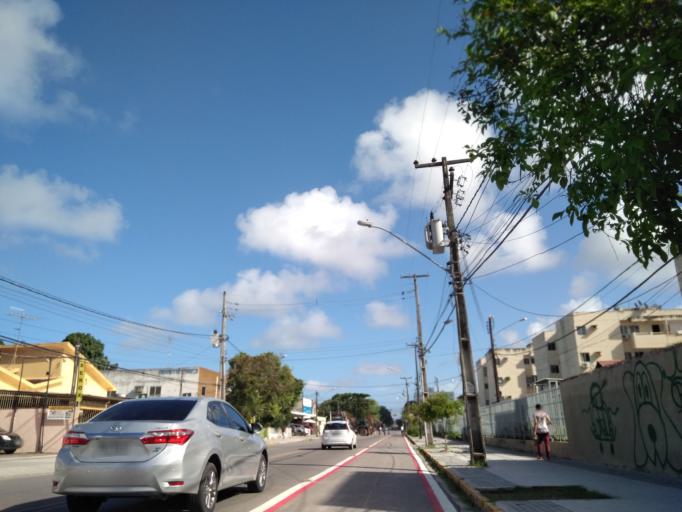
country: BR
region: Pernambuco
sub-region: Recife
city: Recife
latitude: -8.0915
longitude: -34.9108
